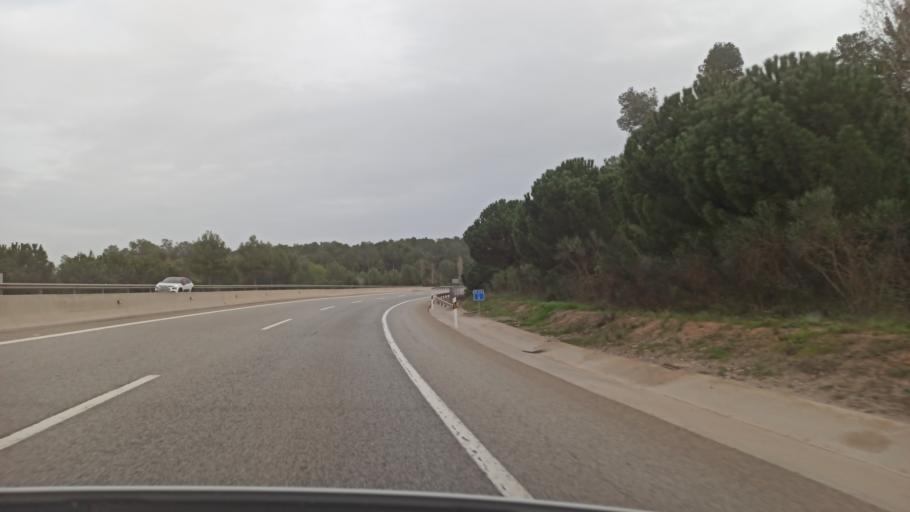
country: ES
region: Catalonia
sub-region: Provincia de Barcelona
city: Cervello
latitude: 41.3921
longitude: 1.9559
